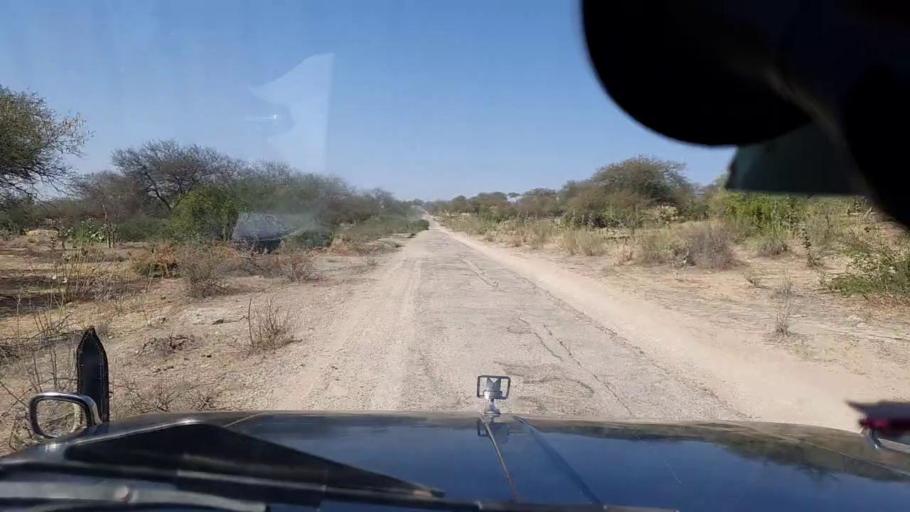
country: PK
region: Sindh
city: Mithi
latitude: 24.6117
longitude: 69.7041
